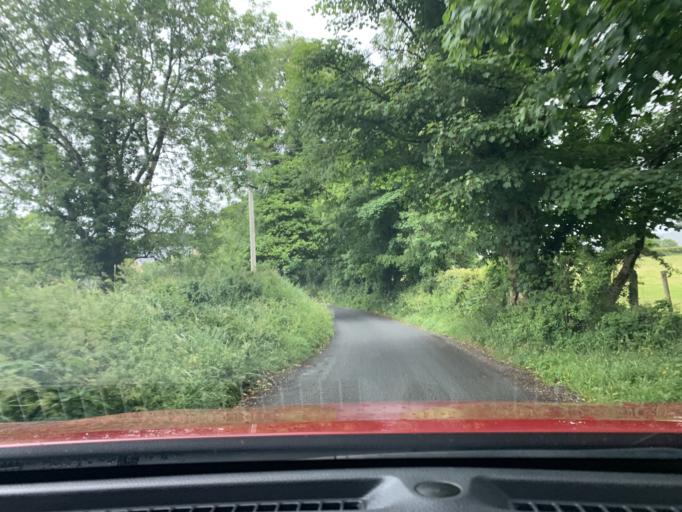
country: IE
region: Connaught
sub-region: Sligo
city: Sligo
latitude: 54.3031
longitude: -8.4570
